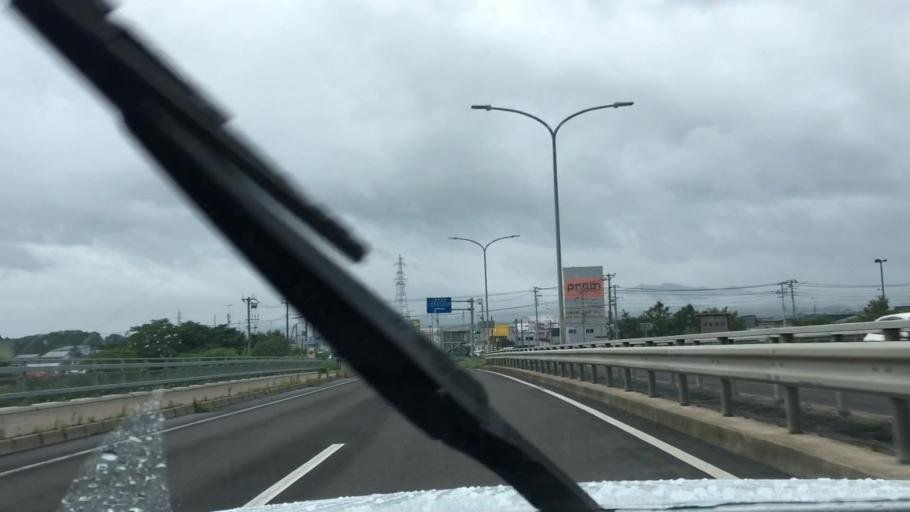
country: JP
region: Hokkaido
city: Nanae
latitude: 42.2626
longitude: 140.2740
